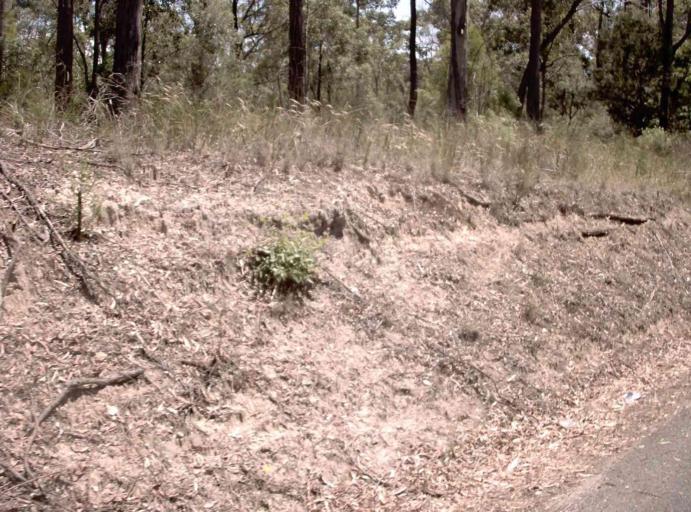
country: AU
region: Victoria
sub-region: East Gippsland
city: Lakes Entrance
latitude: -37.8241
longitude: 148.0322
